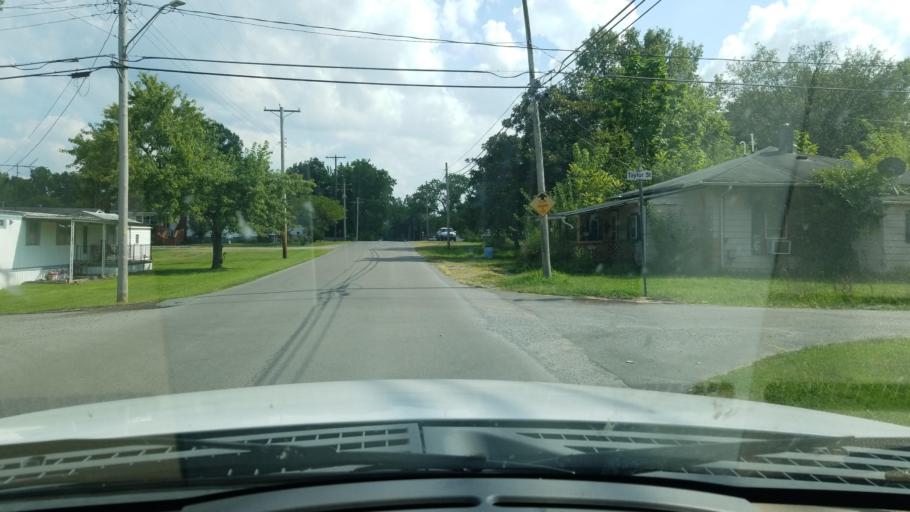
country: US
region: Illinois
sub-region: Saline County
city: Eldorado
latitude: 37.8242
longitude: -88.4363
